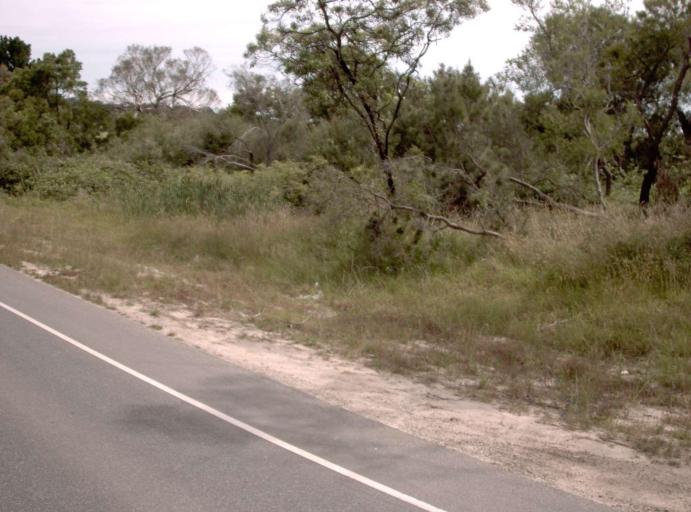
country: AU
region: Victoria
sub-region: Mornington Peninsula
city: Mount Martha
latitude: -38.2725
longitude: 145.0711
